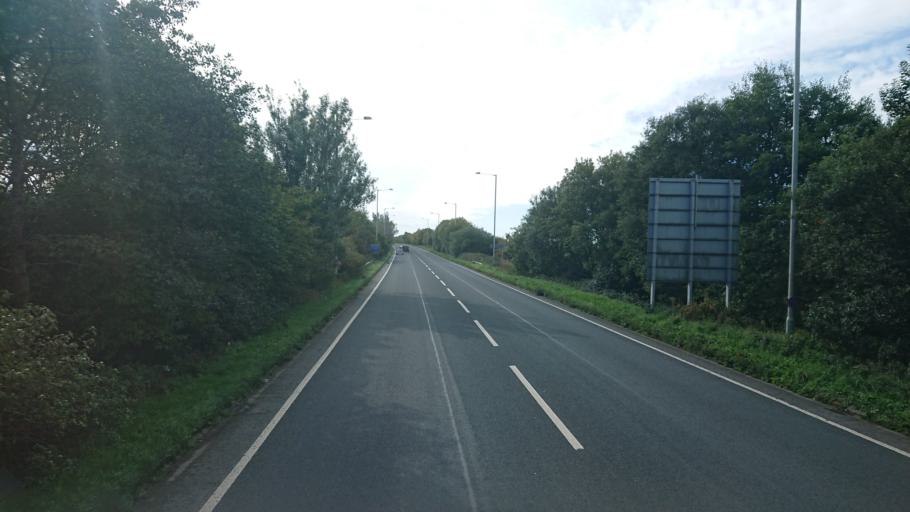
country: GB
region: England
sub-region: Lancashire
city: Morecambe
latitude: 54.0534
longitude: -2.8412
